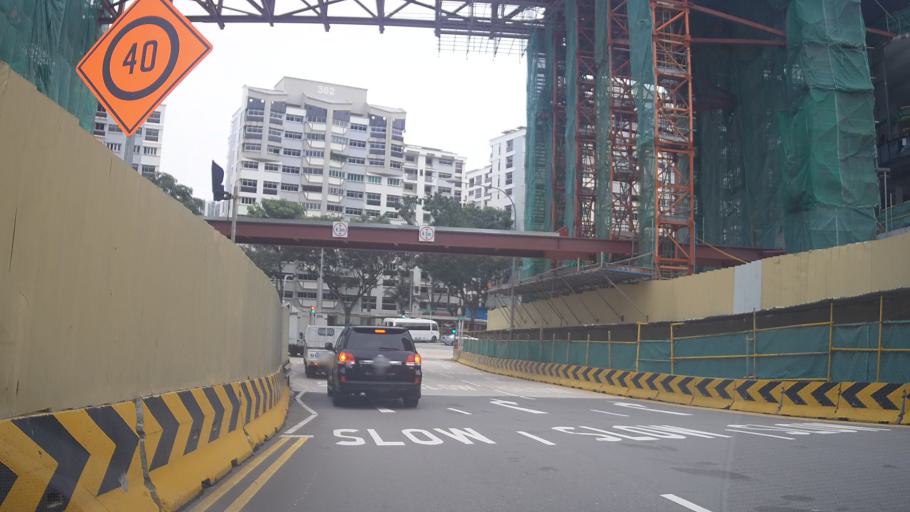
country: MY
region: Johor
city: Johor Bahru
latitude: 1.4353
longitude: 103.7862
